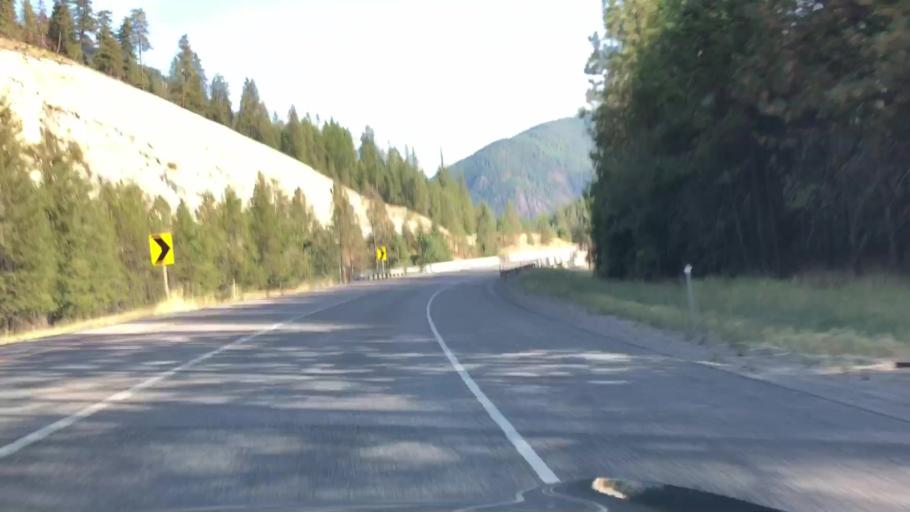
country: US
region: Montana
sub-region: Sanders County
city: Thompson Falls
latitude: 47.3307
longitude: -115.2597
